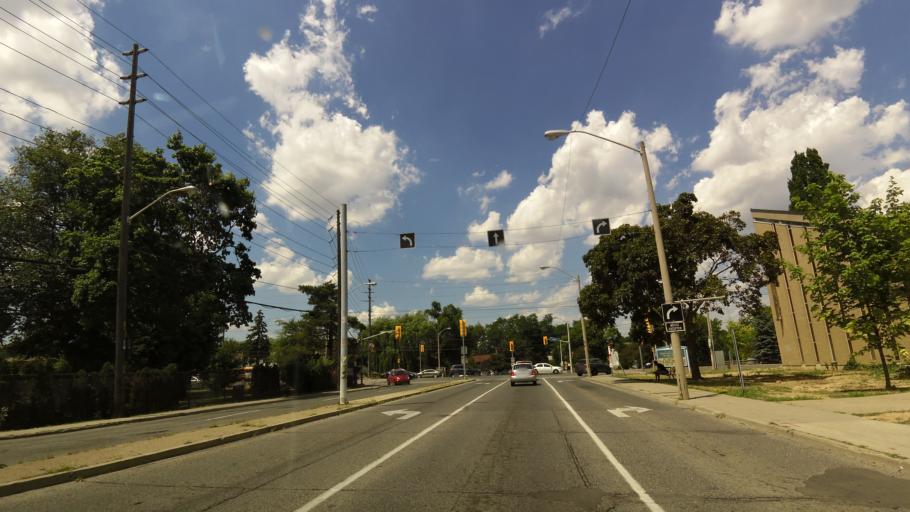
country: CA
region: Ontario
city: Etobicoke
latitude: 43.6993
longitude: -79.5339
